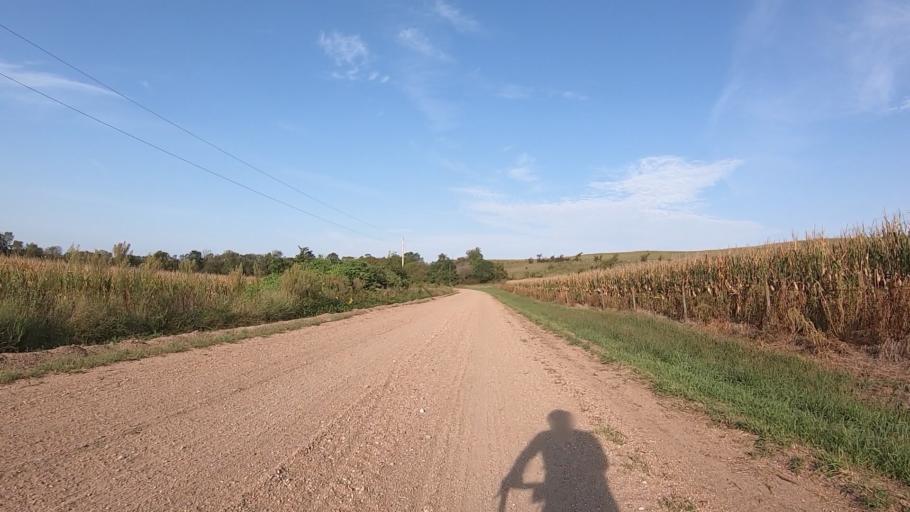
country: US
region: Kansas
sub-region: Marshall County
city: Blue Rapids
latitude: 39.6678
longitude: -96.8106
